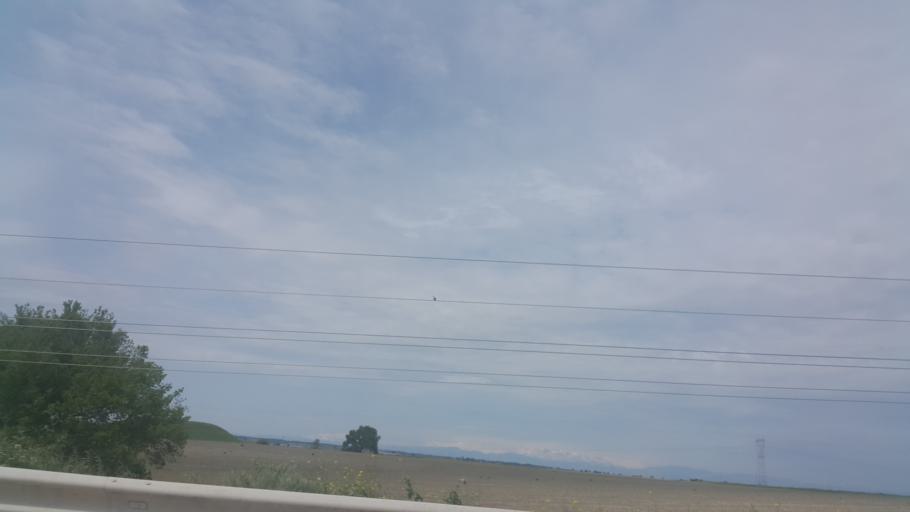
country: TR
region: Adana
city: Ceyhan
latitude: 37.0174
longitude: 35.7164
